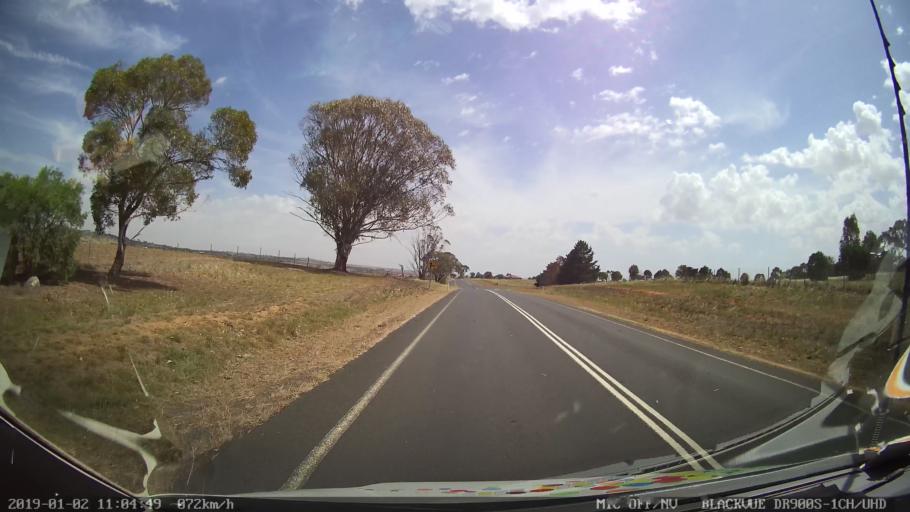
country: AU
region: New South Wales
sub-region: Young
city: Young
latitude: -34.5722
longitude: 148.3538
